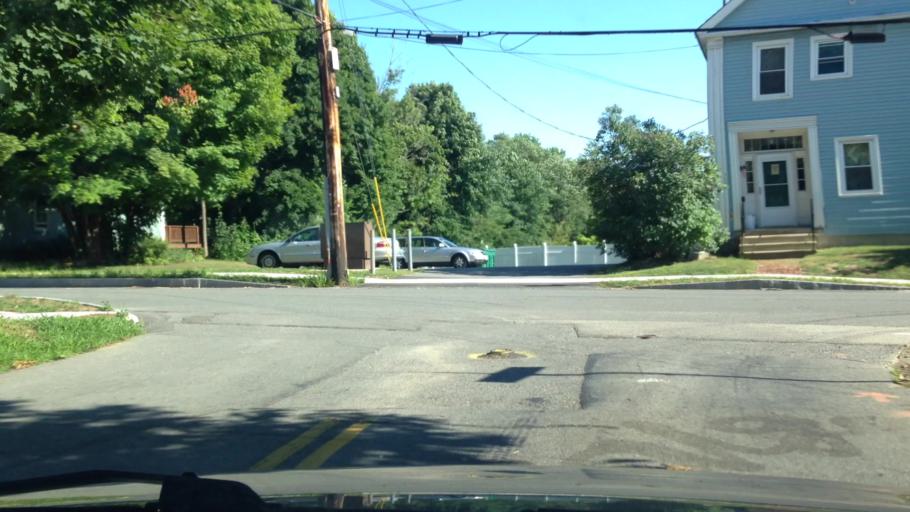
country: US
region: New Hampshire
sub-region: Cheshire County
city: Keene
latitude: 42.9311
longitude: -72.2661
